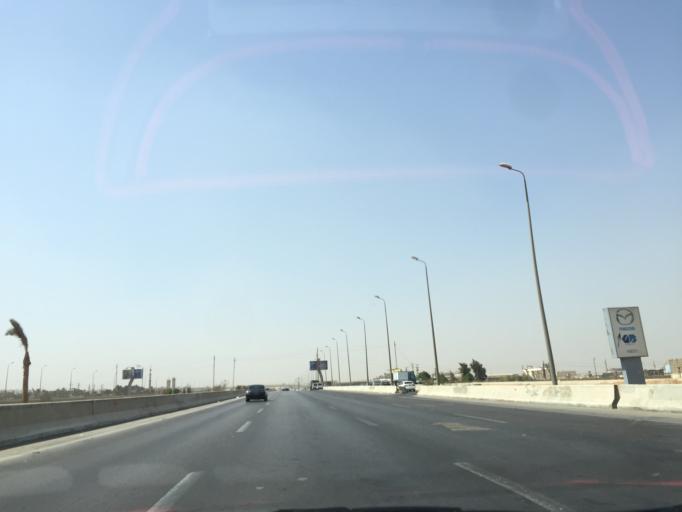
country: EG
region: Al Jizah
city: Awsim
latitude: 30.0726
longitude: 31.0099
